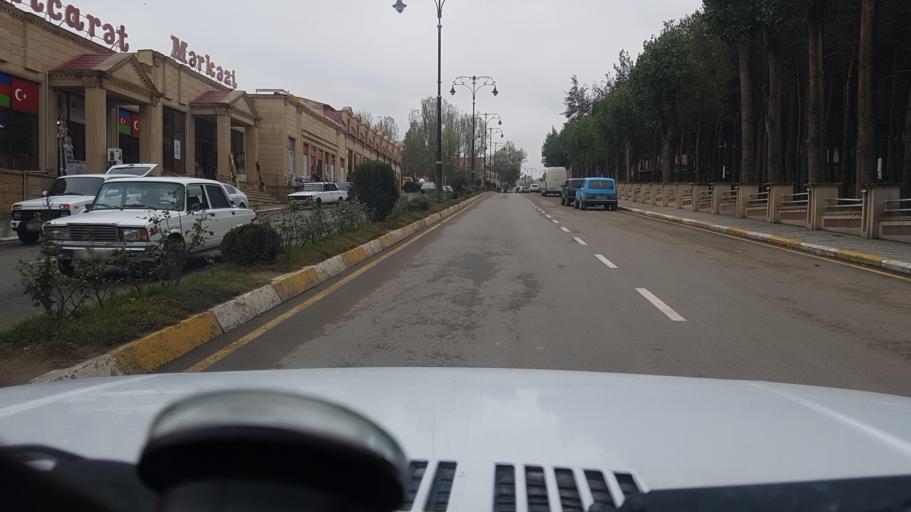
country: AZ
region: Gadabay Rayon
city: Kyadabek
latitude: 40.5790
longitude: 45.8087
